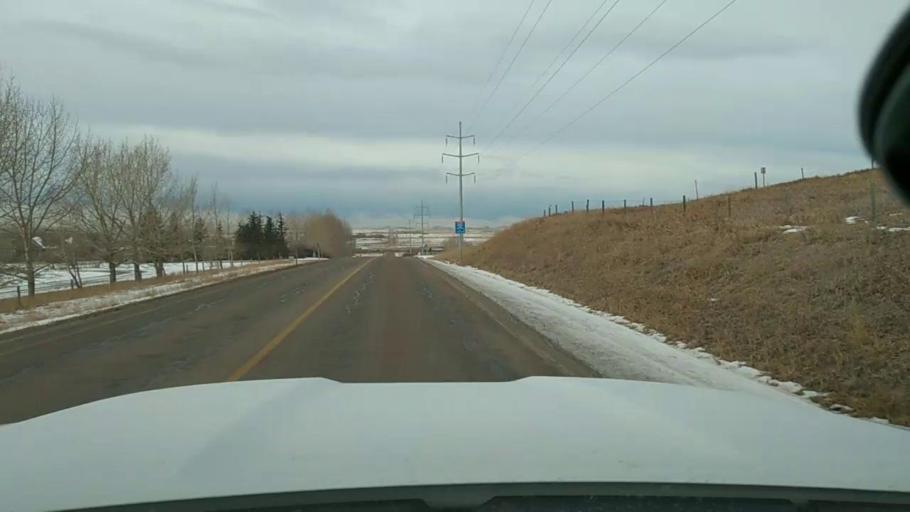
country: CA
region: Alberta
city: Airdrie
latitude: 51.2417
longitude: -113.9857
